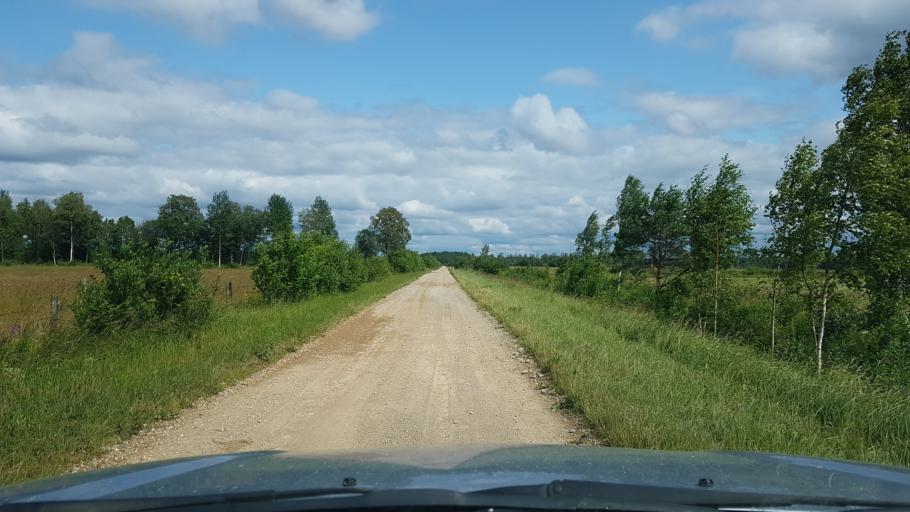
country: EE
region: Ida-Virumaa
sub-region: Sillamaee linn
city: Sillamae
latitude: 59.3703
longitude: 27.9085
